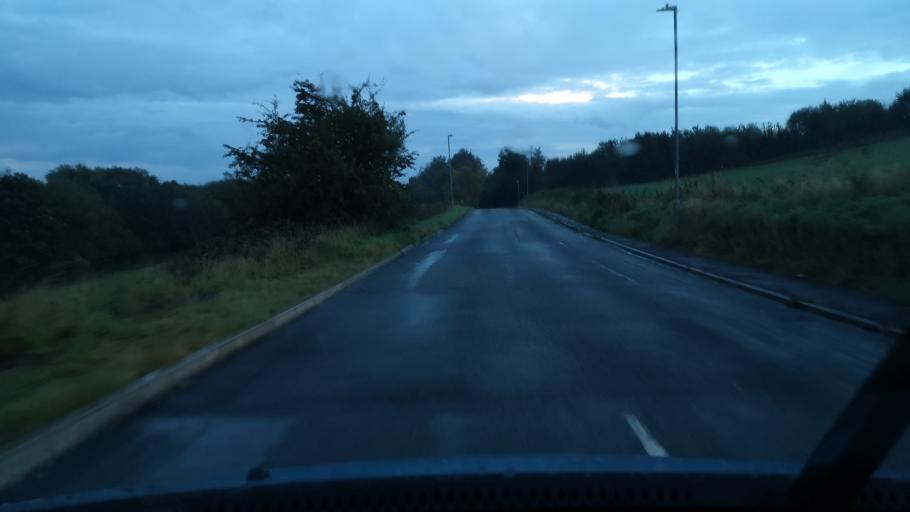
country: GB
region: England
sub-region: Kirklees
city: Batley
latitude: 53.7294
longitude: -1.6384
